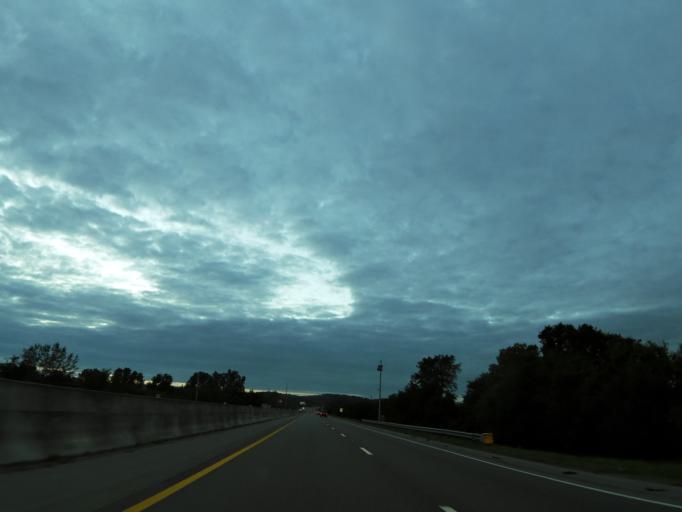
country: US
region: Tennessee
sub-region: Davidson County
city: Nashville
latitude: 36.1943
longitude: -86.8655
